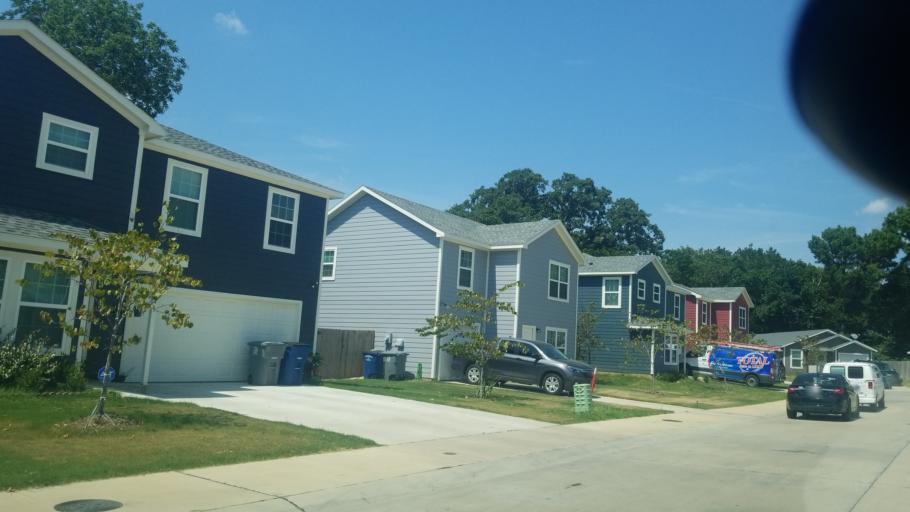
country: US
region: Texas
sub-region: Dallas County
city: Hutchins
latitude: 32.7165
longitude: -96.7462
